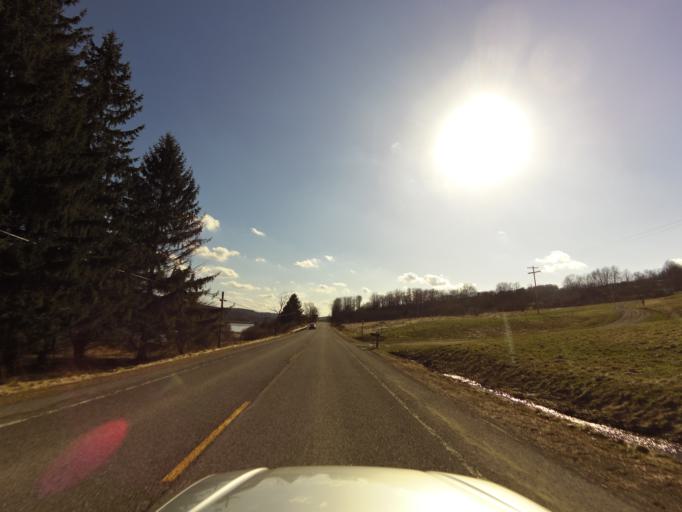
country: US
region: New York
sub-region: Cattaraugus County
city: Franklinville
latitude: 42.3854
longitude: -78.3804
